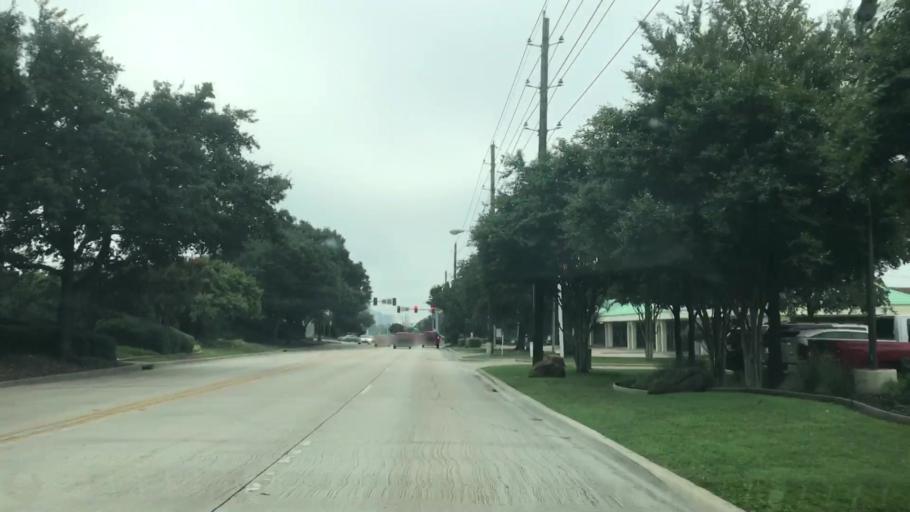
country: US
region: Texas
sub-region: Dallas County
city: Addison
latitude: 32.9492
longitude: -96.8290
